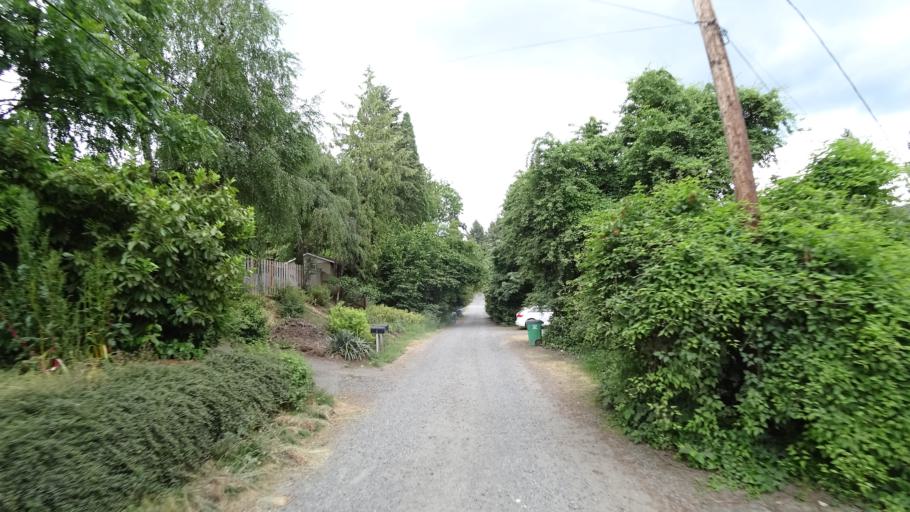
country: US
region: Oregon
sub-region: Clackamas County
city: Lake Oswego
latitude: 45.4591
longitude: -122.6965
